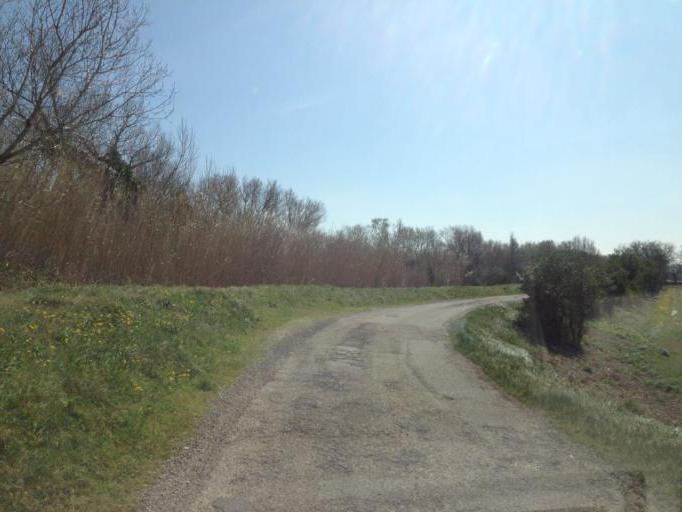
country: FR
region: Provence-Alpes-Cote d'Azur
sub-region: Departement du Vaucluse
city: Sarrians
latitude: 44.0701
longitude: 4.9300
